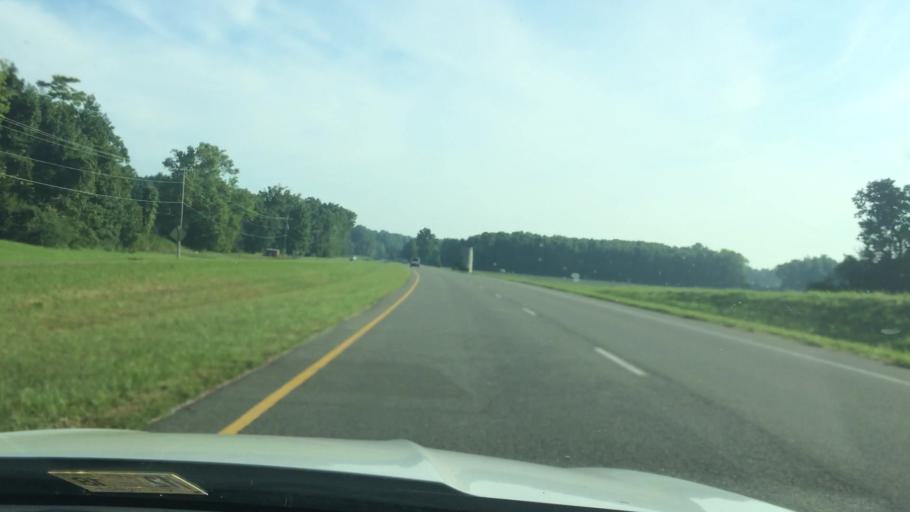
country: US
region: Virginia
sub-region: Gloucester County
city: Gloucester Courthouse
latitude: 37.4402
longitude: -76.4758
